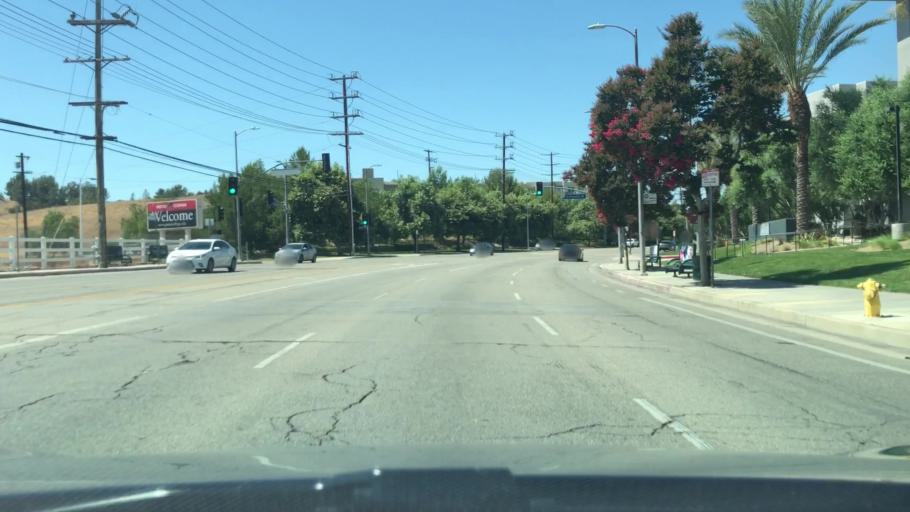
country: US
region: California
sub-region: Los Angeles County
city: Canoga Park
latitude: 34.1853
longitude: -118.5886
